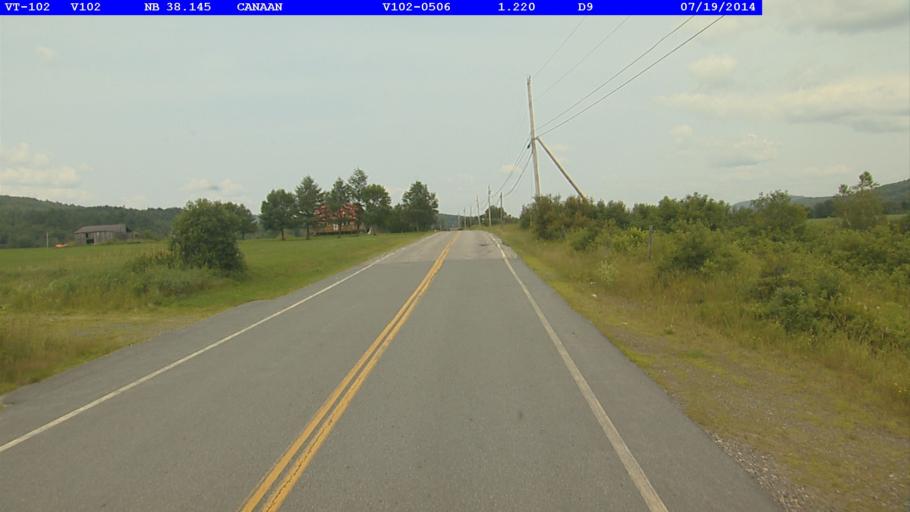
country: US
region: New Hampshire
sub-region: Coos County
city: Colebrook
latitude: 44.9246
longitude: -71.5221
